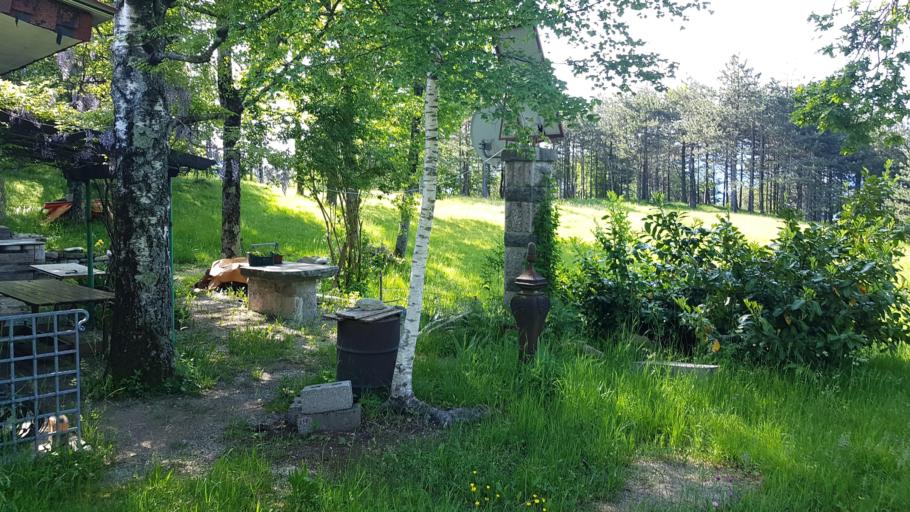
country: IT
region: Friuli Venezia Giulia
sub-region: Provincia di Udine
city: Moggio Udinese
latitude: 46.4267
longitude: 13.1903
